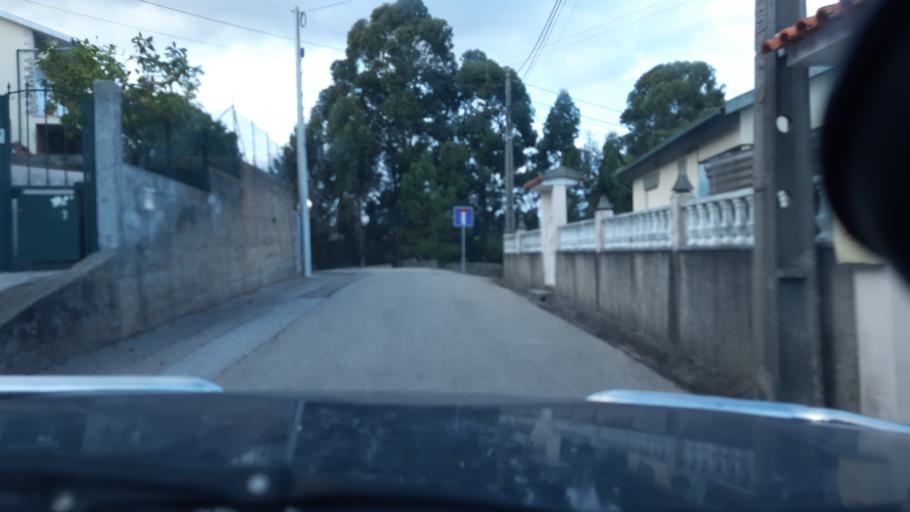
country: PT
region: Aveiro
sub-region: Agueda
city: Agueda
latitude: 40.5775
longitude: -8.4568
